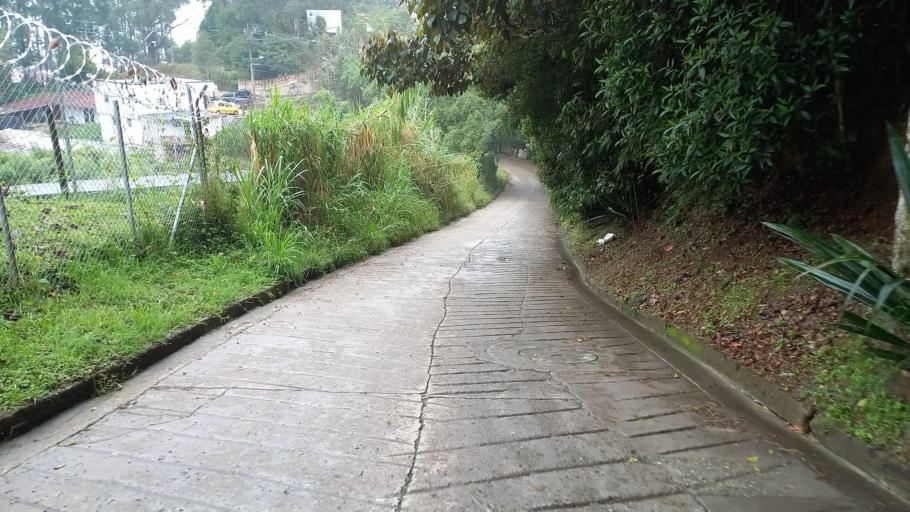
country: CO
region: Antioquia
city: La Estrella
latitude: 6.1676
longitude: -75.6496
